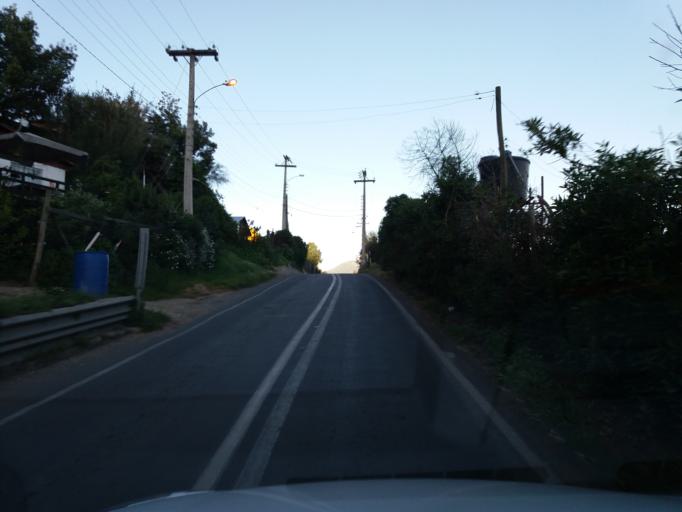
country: CL
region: Valparaiso
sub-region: Provincia de Quillota
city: Quillota
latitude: -32.8770
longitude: -71.2727
